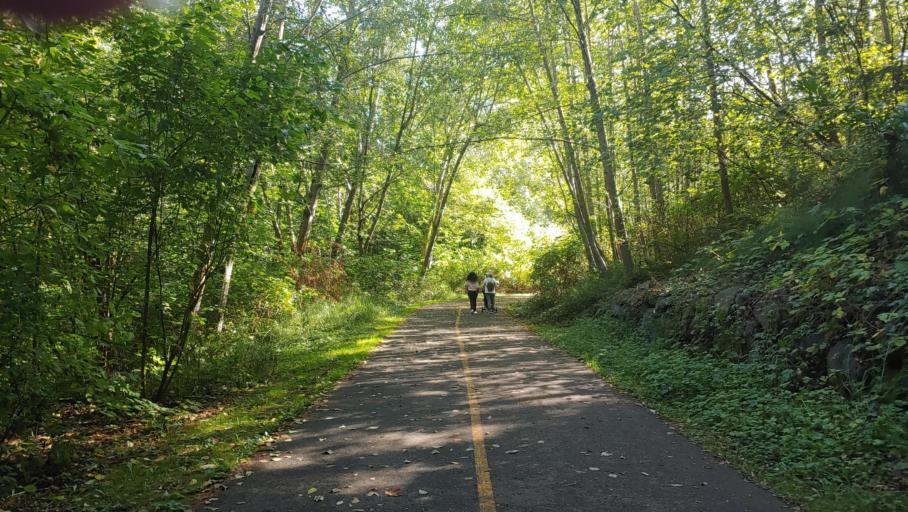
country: US
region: Washington
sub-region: King County
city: Des Moines
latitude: 47.4111
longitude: -122.3243
